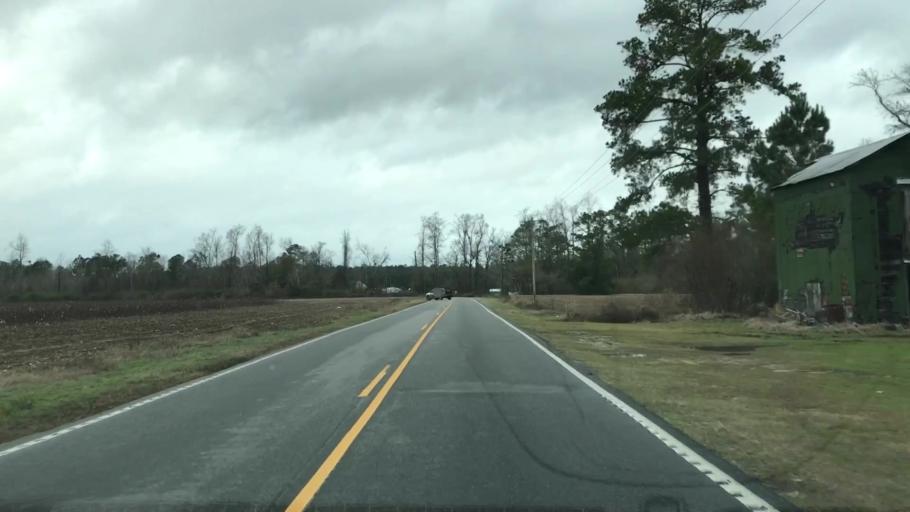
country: US
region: South Carolina
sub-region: Florence County
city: Johnsonville
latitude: 33.6528
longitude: -79.3019
